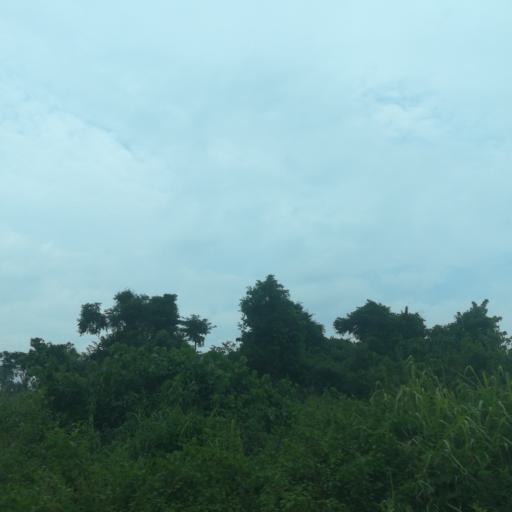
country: NG
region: Lagos
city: Ejirin
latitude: 6.6472
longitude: 3.7524
